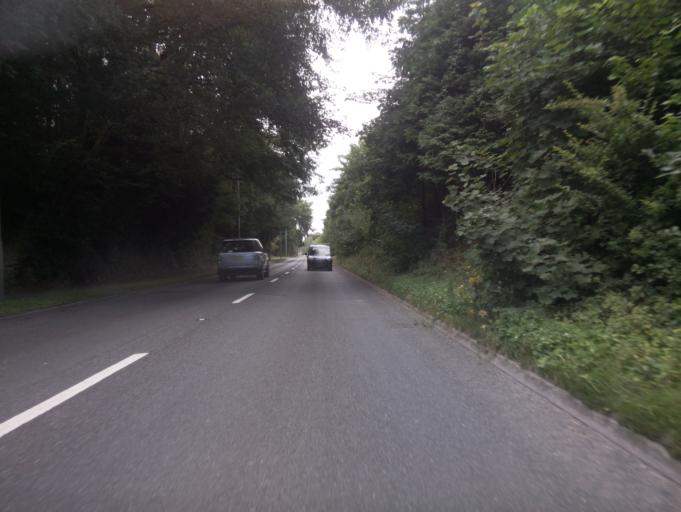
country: GB
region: England
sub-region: Somerset
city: Yeovil
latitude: 50.9251
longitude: -2.6366
